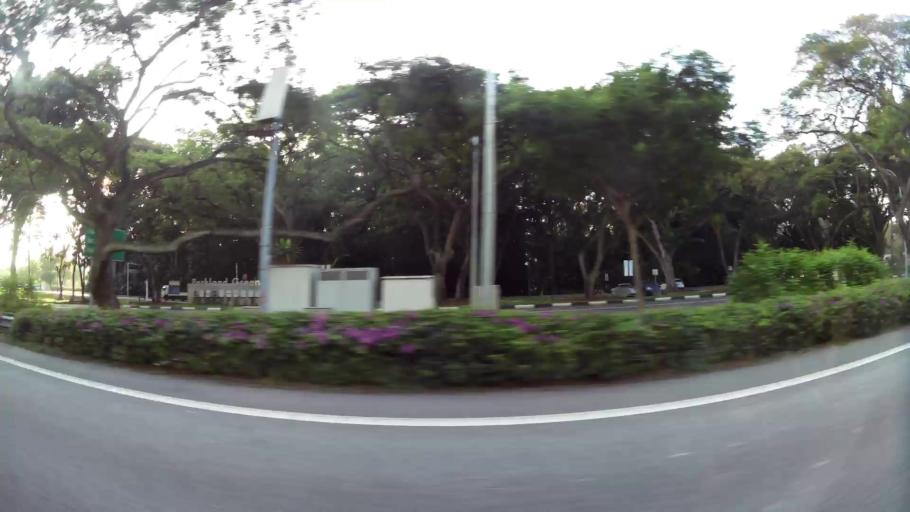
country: SG
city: Singapore
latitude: 1.2995
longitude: 103.9043
